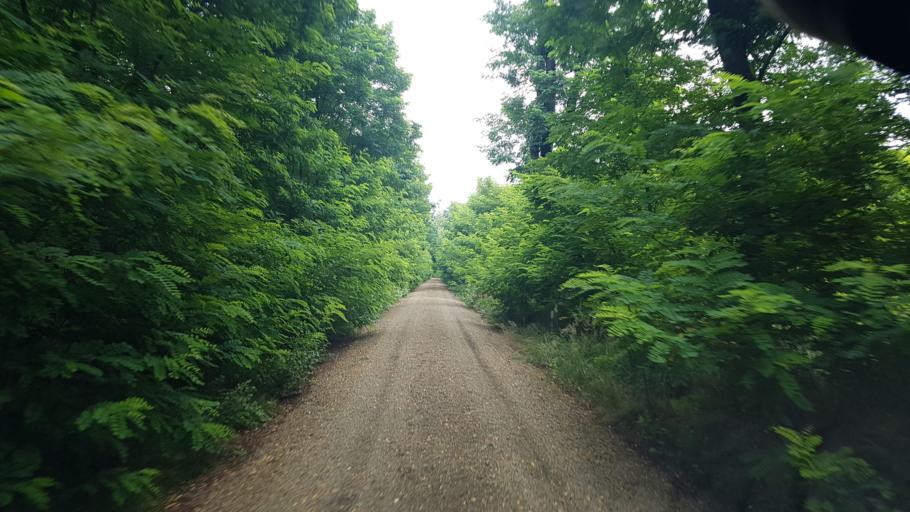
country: DE
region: Brandenburg
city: Altdobern
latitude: 51.6324
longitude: 13.9957
